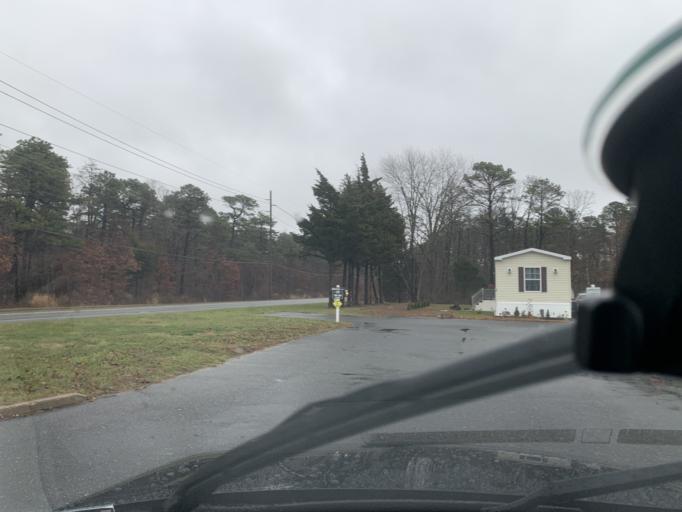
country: US
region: New Jersey
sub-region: Atlantic County
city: Pomona
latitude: 39.4362
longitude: -74.5970
